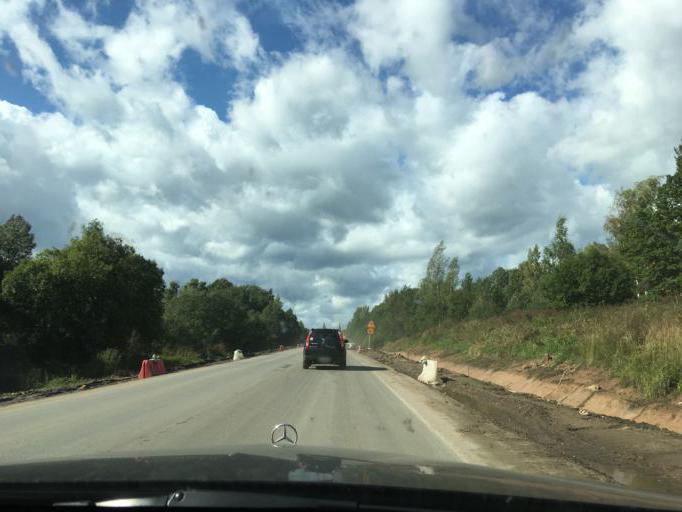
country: RU
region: Pskov
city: Novosokol'niki
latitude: 56.2810
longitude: 30.3018
